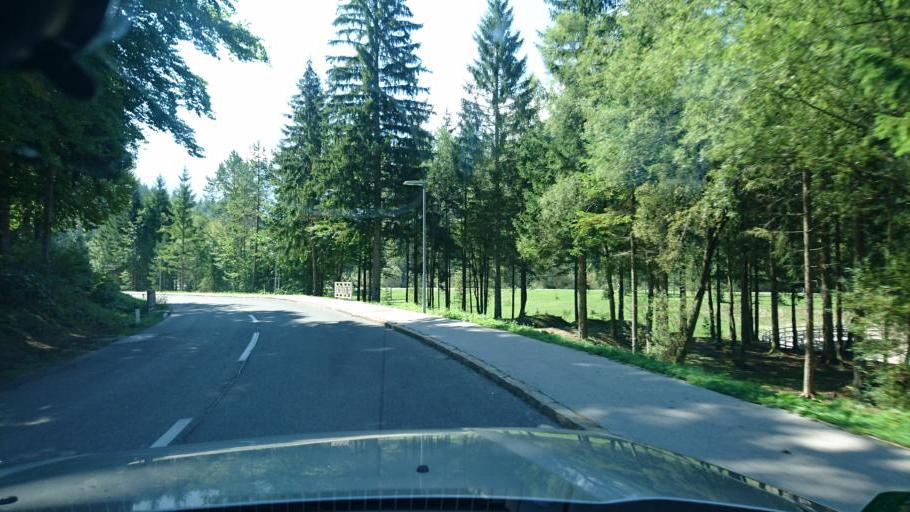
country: SI
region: Kranjska Gora
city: Kranjska Gora
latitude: 46.4731
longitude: 13.7849
